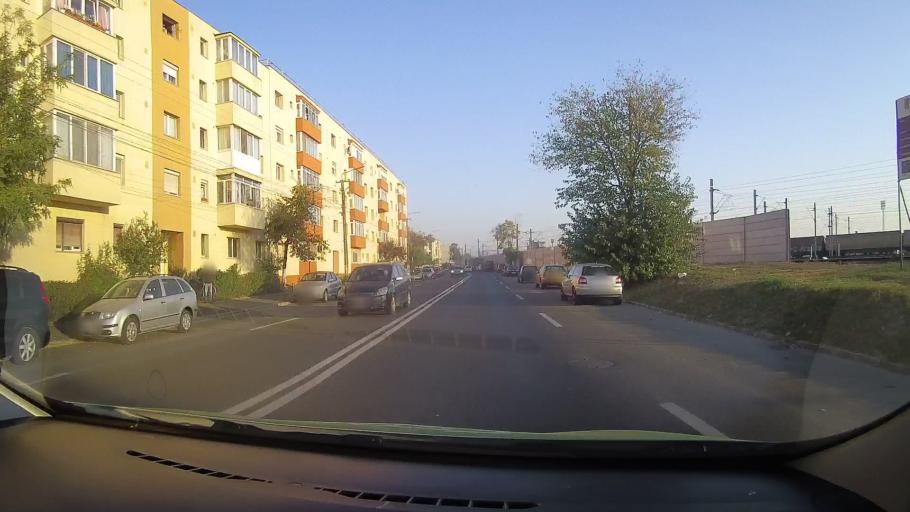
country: RO
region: Arad
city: Arad
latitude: 46.1958
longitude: 21.3206
